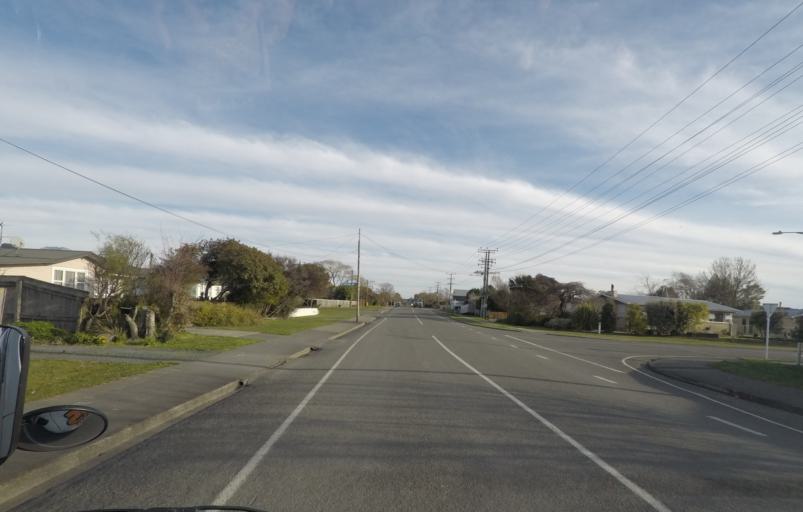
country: NZ
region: Tasman
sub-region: Tasman District
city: Brightwater
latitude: -41.3750
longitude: 173.1055
